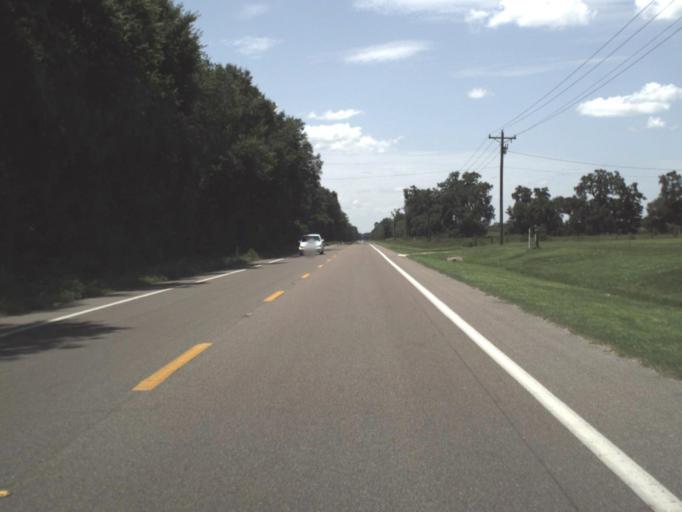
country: US
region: Florida
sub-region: Gilchrist County
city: Trenton
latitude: 29.6471
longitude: -82.8364
